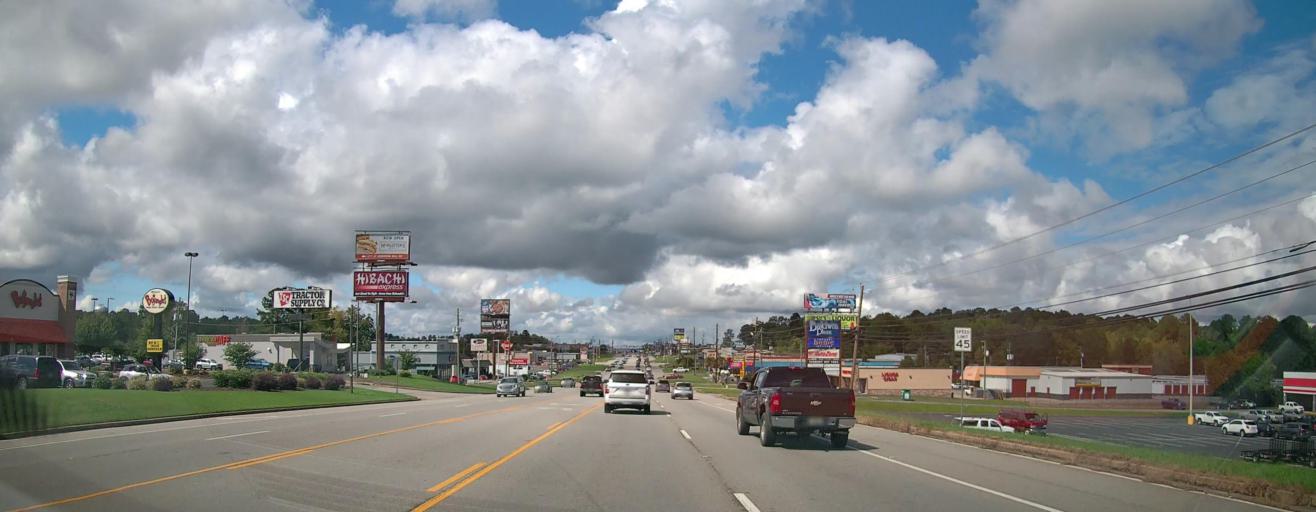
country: US
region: Georgia
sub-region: Baldwin County
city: Milledgeville
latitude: 33.1039
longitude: -83.2502
